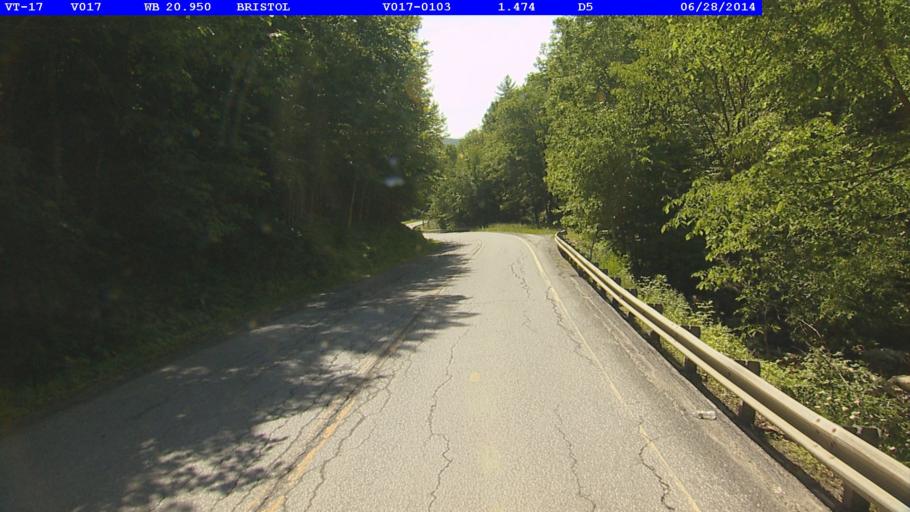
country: US
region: Vermont
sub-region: Addison County
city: Bristol
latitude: 44.1606
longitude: -73.0334
